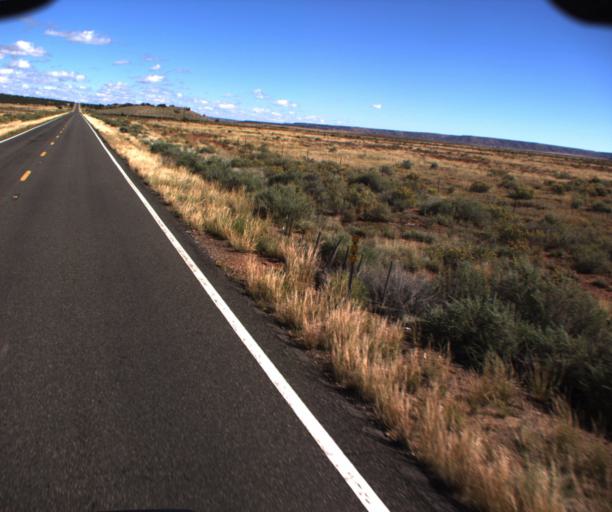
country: US
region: Arizona
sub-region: Apache County
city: Saint Johns
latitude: 34.7119
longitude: -109.2647
